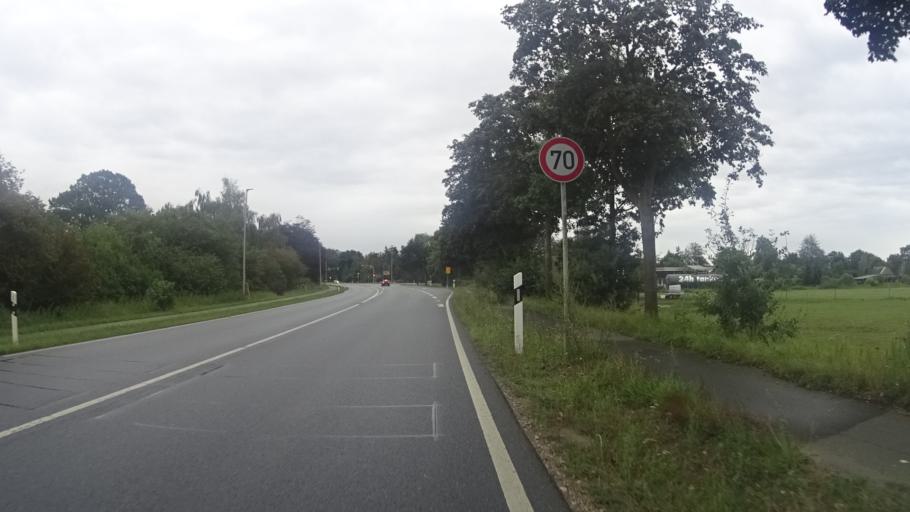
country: DE
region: Schleswig-Holstein
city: Kiebitzreihe
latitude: 53.7831
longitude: 9.6380
